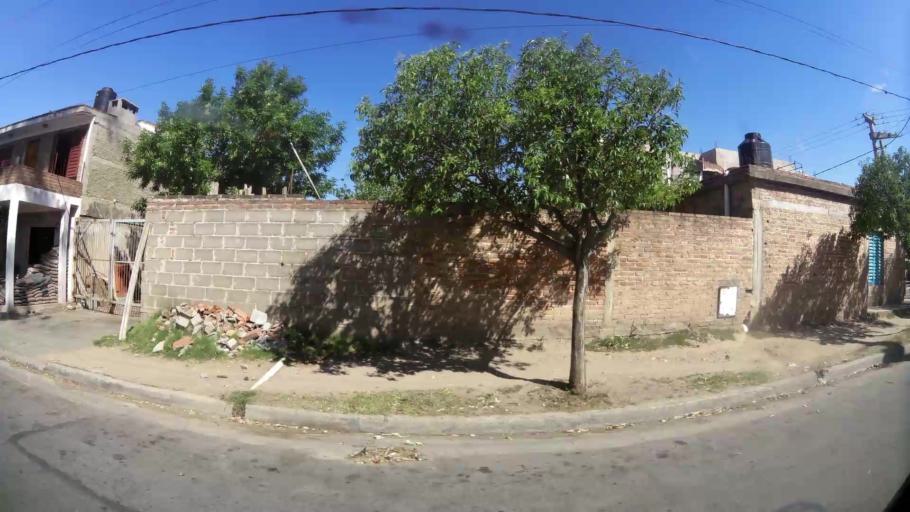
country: AR
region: Cordoba
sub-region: Departamento de Capital
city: Cordoba
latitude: -31.3657
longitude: -64.1666
